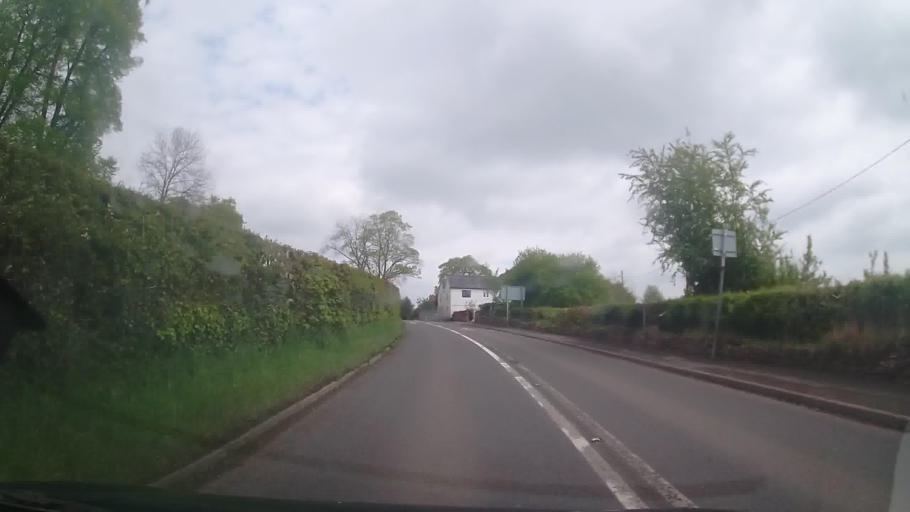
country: GB
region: Wales
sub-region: Wrexham
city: Overton
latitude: 52.9781
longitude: -2.9634
